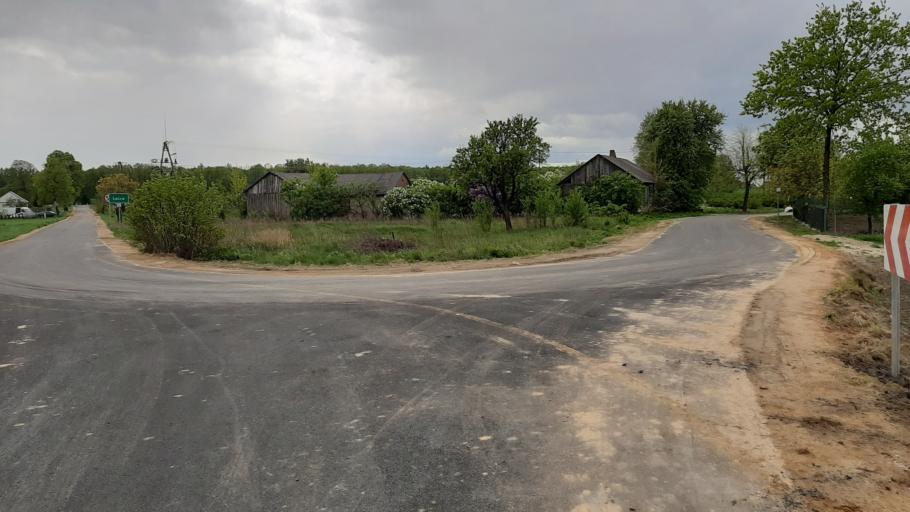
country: PL
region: Lublin Voivodeship
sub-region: Powiat lubelski
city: Garbow
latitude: 51.3801
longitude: 22.4019
